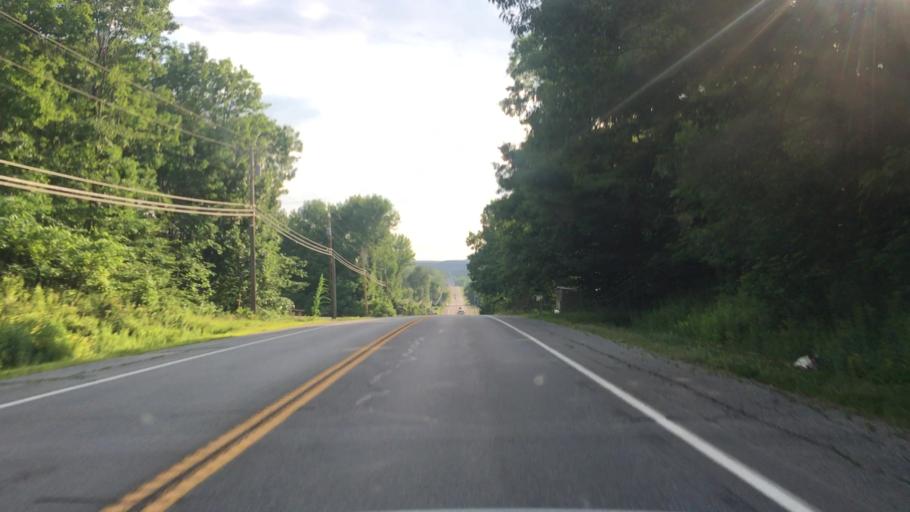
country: US
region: Maine
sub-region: Kennebec County
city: Augusta
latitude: 44.3336
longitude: -69.7083
